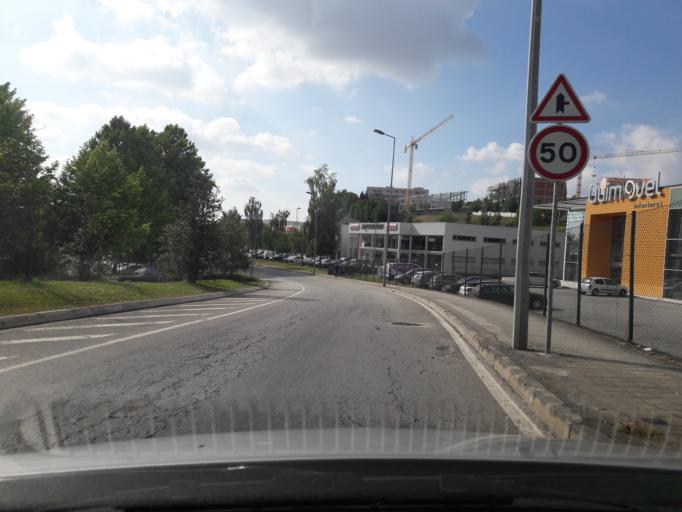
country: PT
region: Braga
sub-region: Guimaraes
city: Urgeses
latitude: 41.4232
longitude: -8.3009
